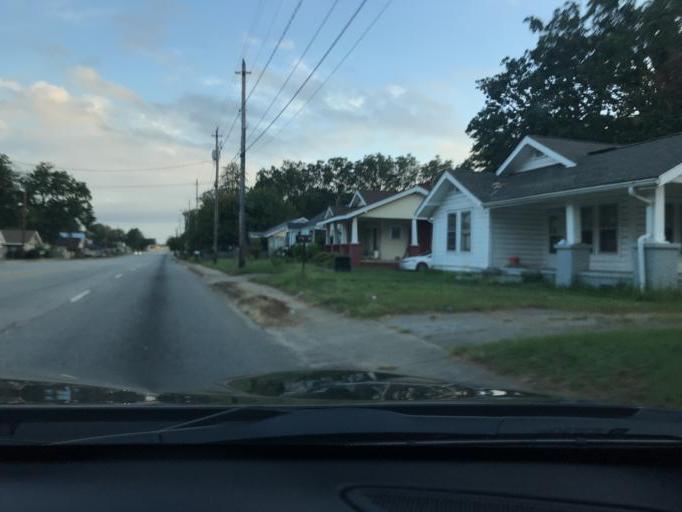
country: US
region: South Carolina
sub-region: Greenville County
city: Welcome
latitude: 34.8360
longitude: -82.4413
